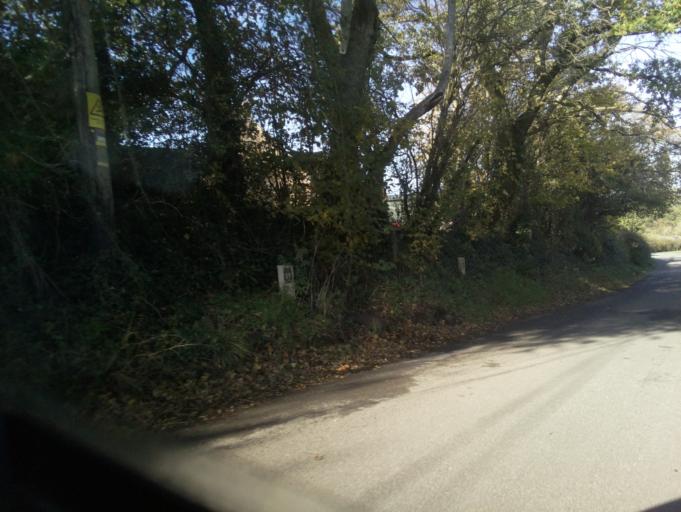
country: GB
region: England
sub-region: Somerset
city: Yeovil
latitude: 50.8852
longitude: -2.5781
